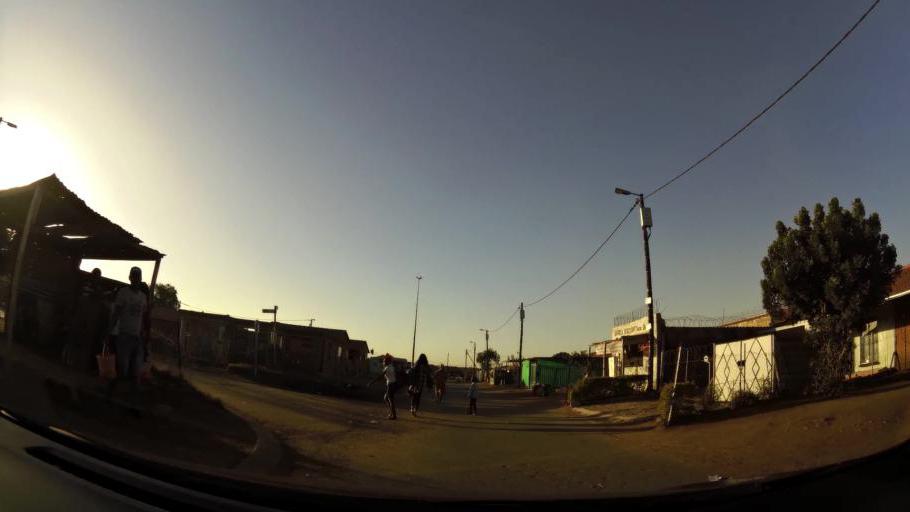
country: ZA
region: Gauteng
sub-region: City of Tshwane Metropolitan Municipality
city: Mabopane
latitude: -25.6041
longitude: 28.1097
